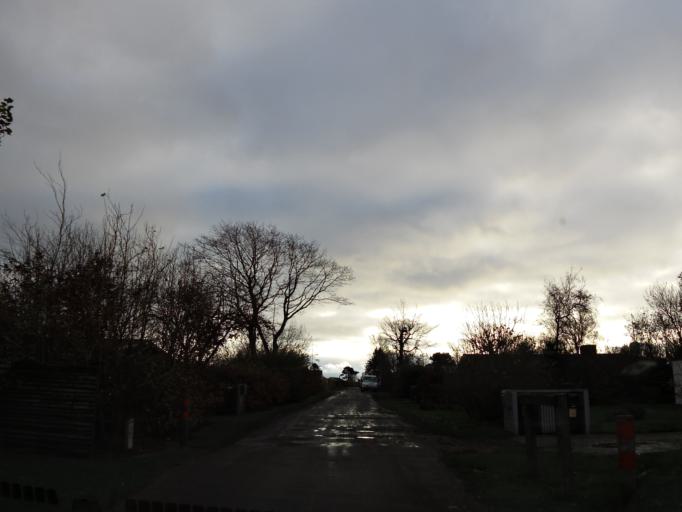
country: DK
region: Central Jutland
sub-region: Arhus Kommune
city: Malling
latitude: 55.9600
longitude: 10.2636
